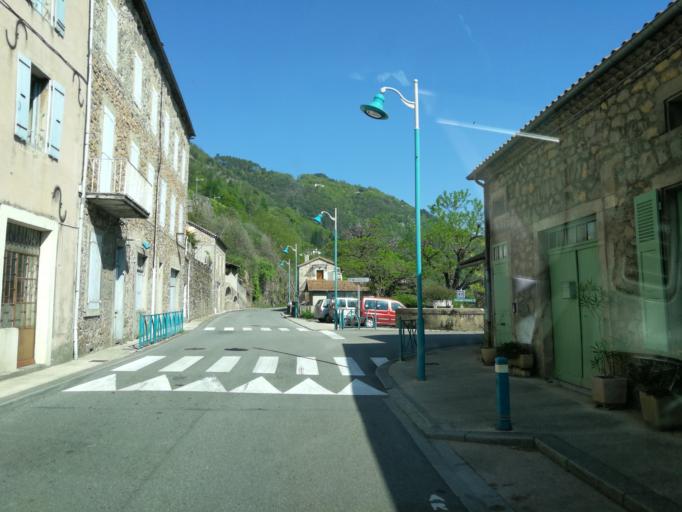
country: FR
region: Rhone-Alpes
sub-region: Departement de l'Ardeche
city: Saint-Sauveur-de-Montagut
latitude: 44.8231
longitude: 4.5796
